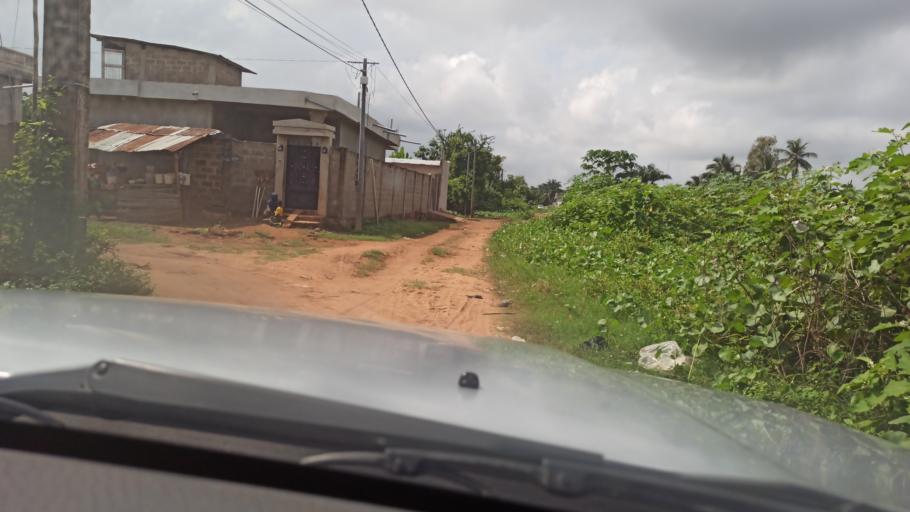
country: BJ
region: Queme
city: Porto-Novo
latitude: 6.4658
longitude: 2.6455
